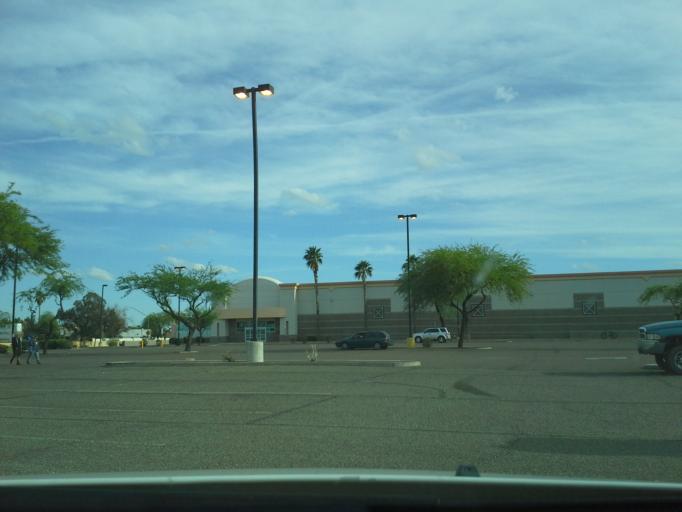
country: US
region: Arizona
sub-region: Maricopa County
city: Peoria
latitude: 33.6372
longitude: -112.2039
